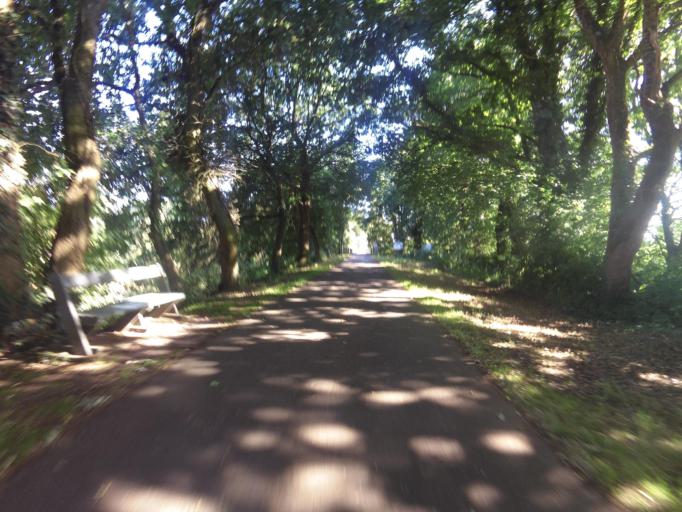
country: FR
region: Brittany
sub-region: Departement du Morbihan
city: Guillac
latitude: 47.8681
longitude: -2.4382
